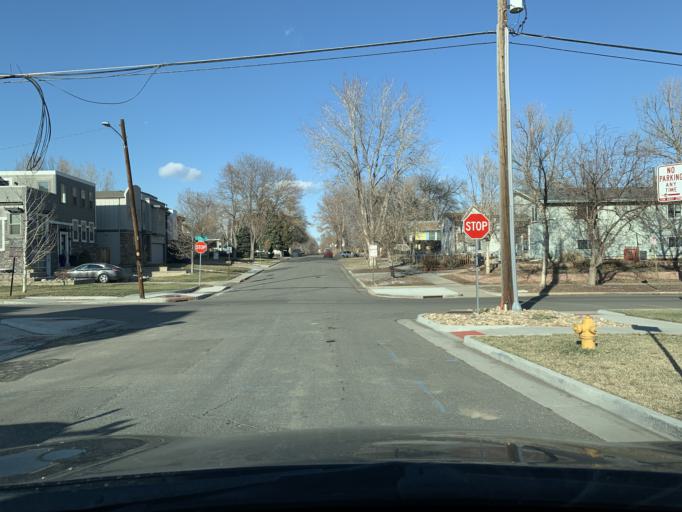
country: US
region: Colorado
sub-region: Jefferson County
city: Edgewater
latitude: 39.7474
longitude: -105.0284
